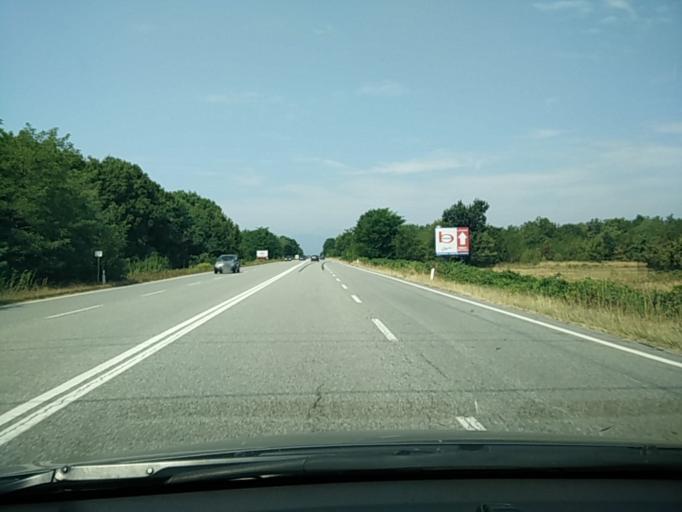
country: IT
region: Piedmont
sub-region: Provincia di Torino
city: Volpiano
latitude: 45.1885
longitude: 7.7626
